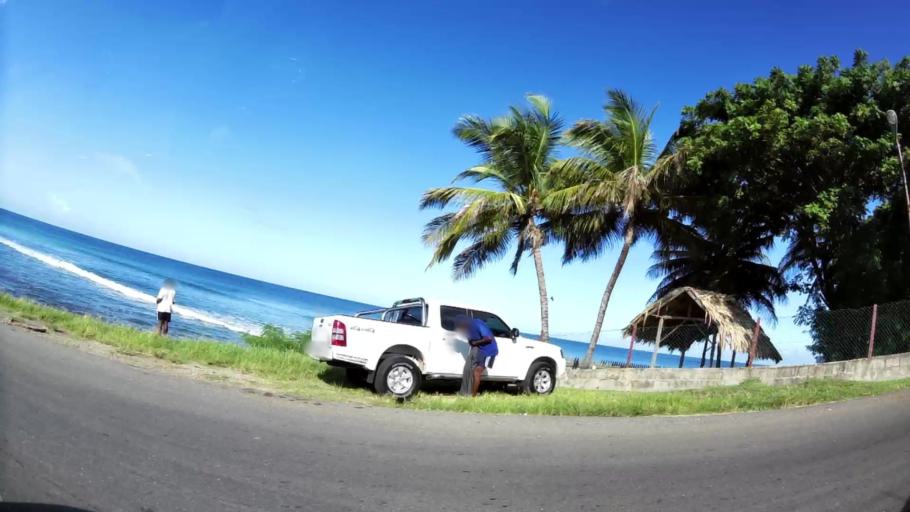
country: TT
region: Tobago
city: Scarborough
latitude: 11.1514
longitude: -60.8455
